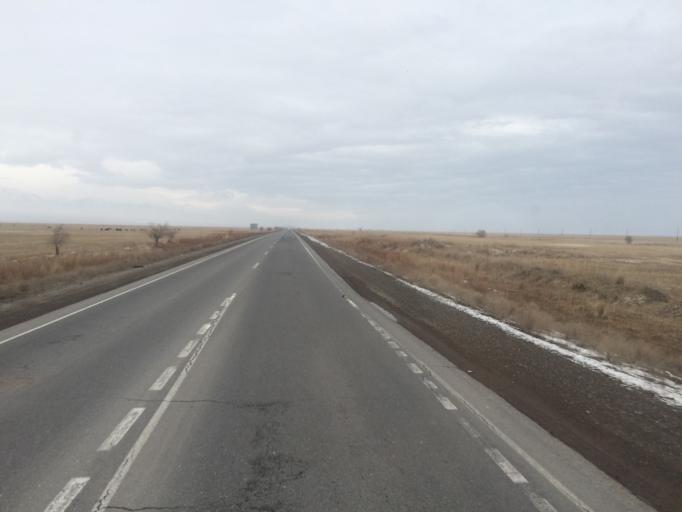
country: KG
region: Chuy
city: Tokmok
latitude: 43.3517
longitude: 75.4631
